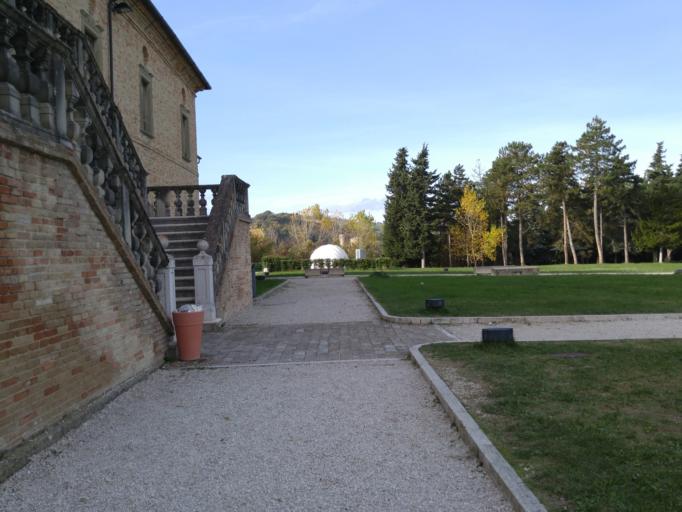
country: IT
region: The Marches
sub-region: Provincia di Pesaro e Urbino
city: Saltara
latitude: 43.7562
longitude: 12.8904
